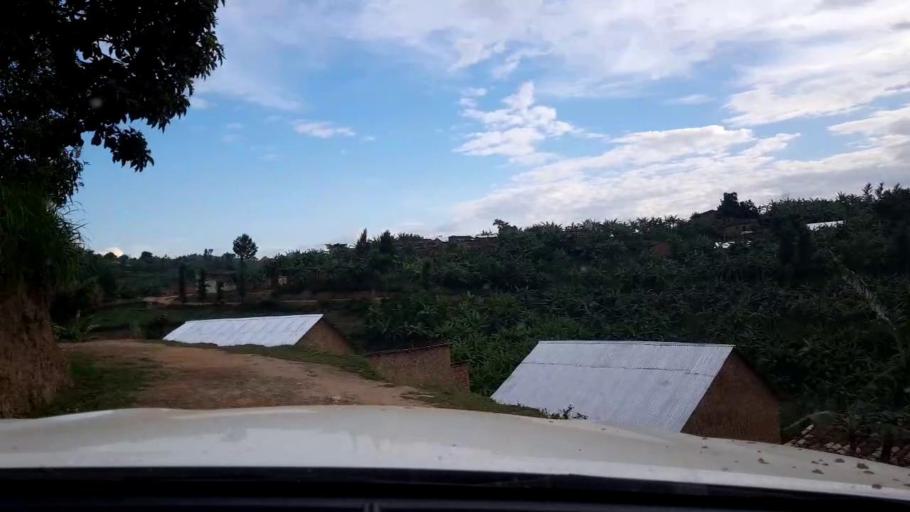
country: RW
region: Western Province
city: Kibuye
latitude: -2.0003
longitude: 29.3692
